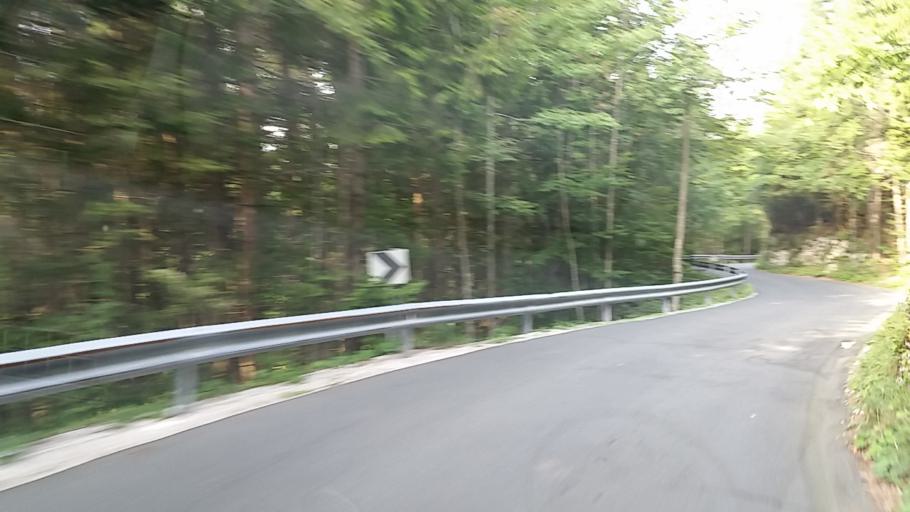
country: SI
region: Bohinj
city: Bohinjska Bistrica
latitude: 46.2707
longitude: 14.0185
